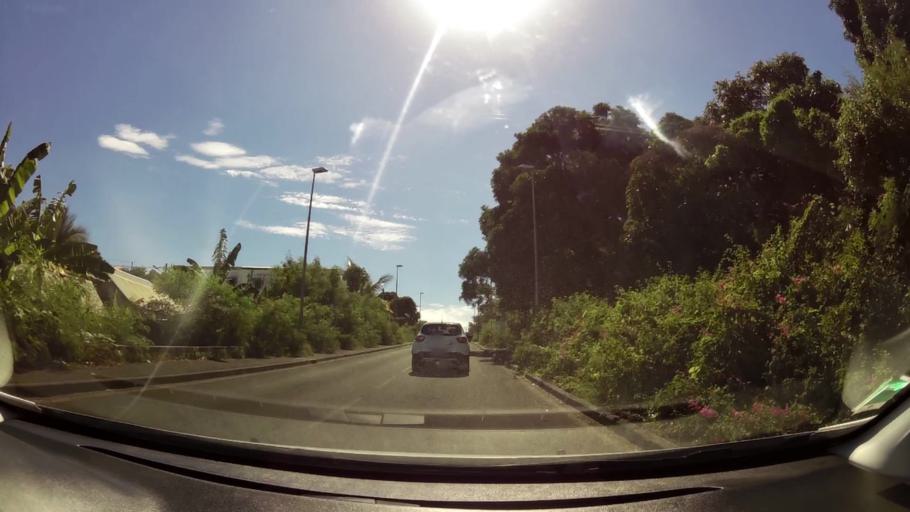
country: YT
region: Pamandzi
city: Pamandzi
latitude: -12.8001
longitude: 45.2835
